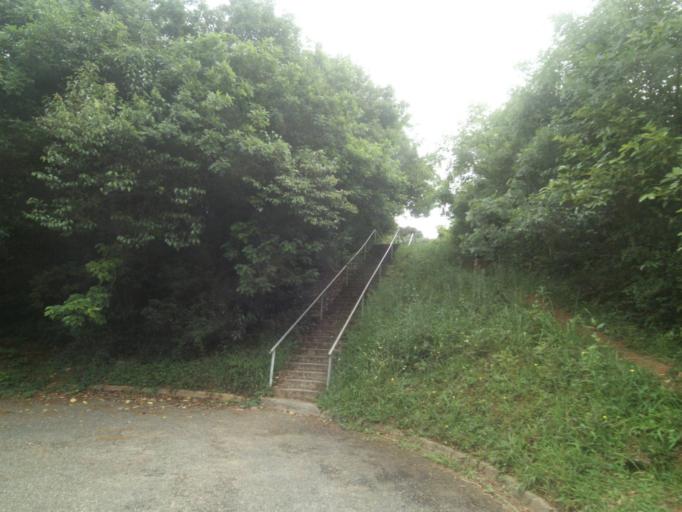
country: BR
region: Parana
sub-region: Curitiba
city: Curitiba
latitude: -25.4140
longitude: -49.3045
